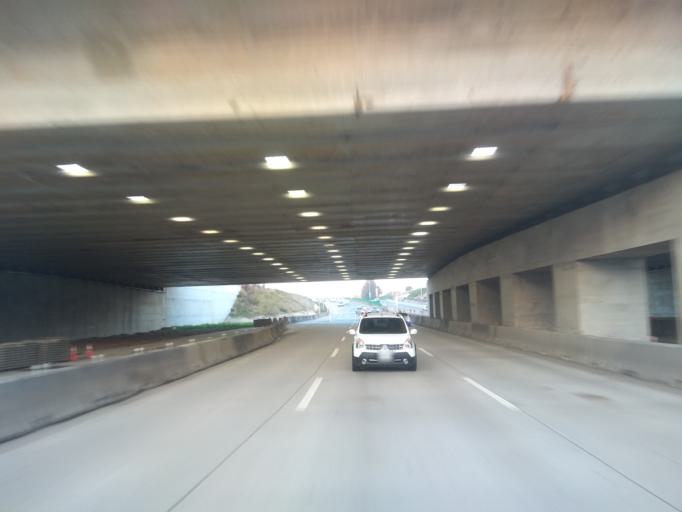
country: TW
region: Taiwan
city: Taoyuan City
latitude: 25.0693
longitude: 121.2241
